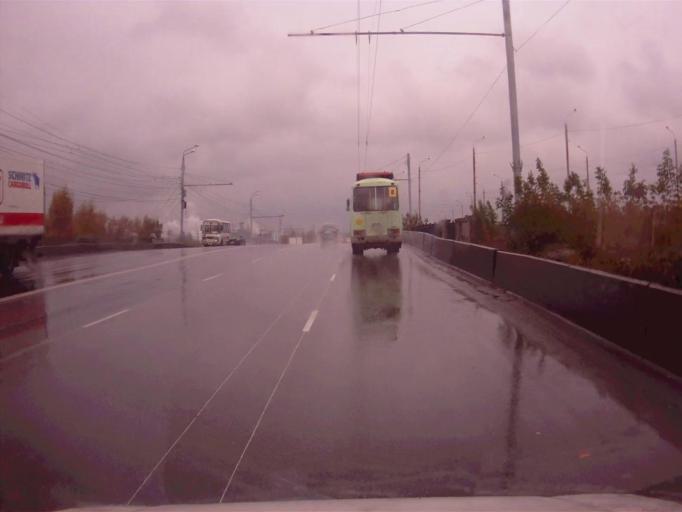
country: RU
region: Chelyabinsk
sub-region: Gorod Chelyabinsk
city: Chelyabinsk
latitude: 55.1970
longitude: 61.3861
